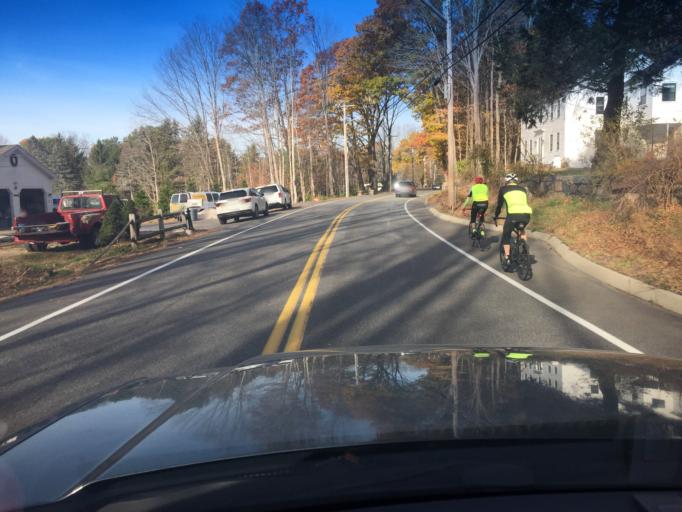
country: US
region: Maine
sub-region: York County
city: York Harbor
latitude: 43.1562
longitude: -70.6922
